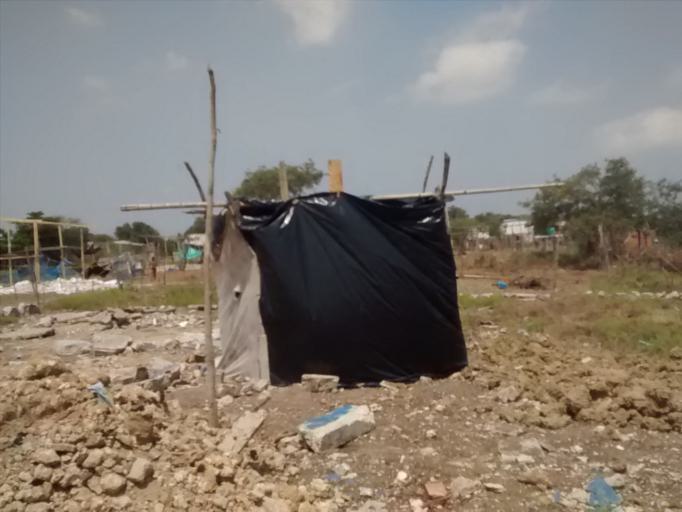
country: CO
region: Bolivar
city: Cartagena
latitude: 10.4148
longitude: -75.4678
